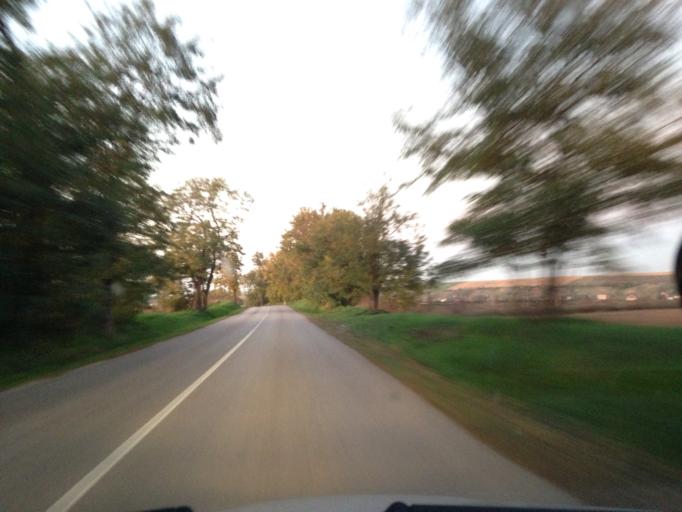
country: SK
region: Nitriansky
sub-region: Okres Komarno
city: Hurbanovo
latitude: 47.8566
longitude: 18.2738
